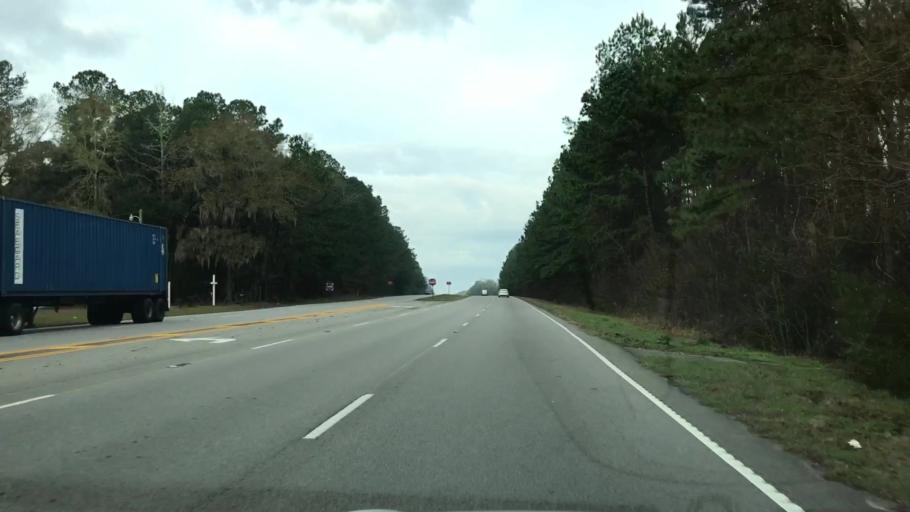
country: US
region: South Carolina
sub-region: Hampton County
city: Yemassee
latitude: 32.6268
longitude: -80.8289
